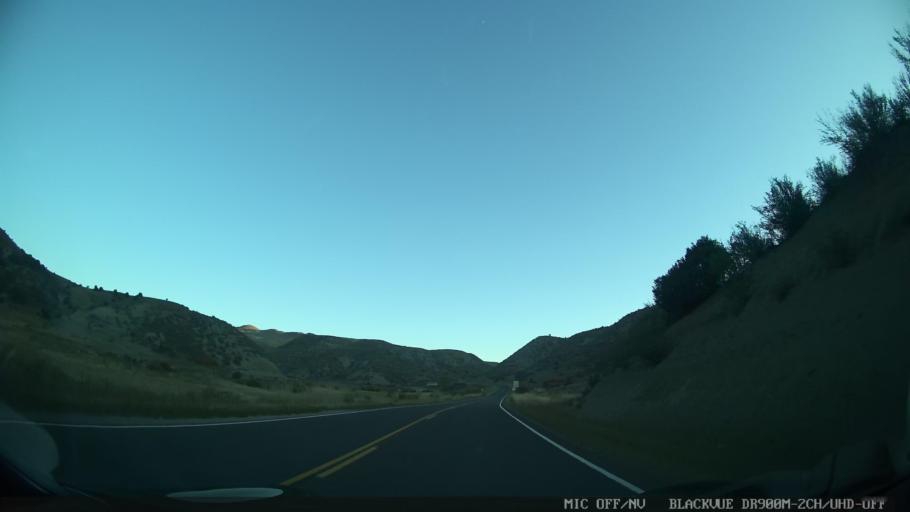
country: US
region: Colorado
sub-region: Eagle County
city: Edwards
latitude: 39.7933
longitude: -106.6799
